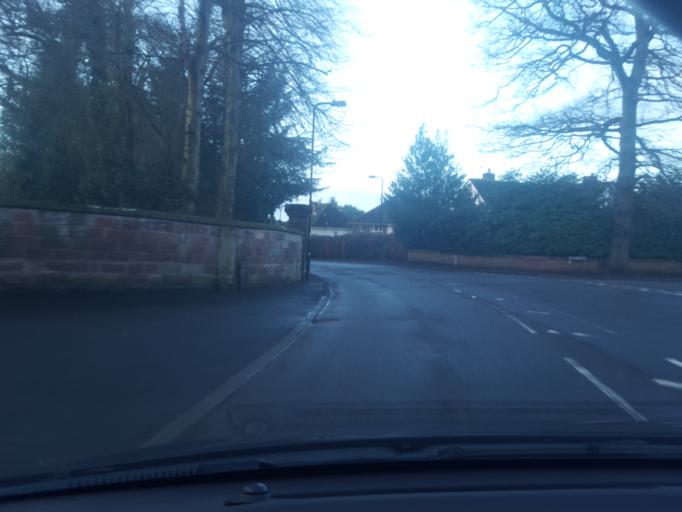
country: GB
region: England
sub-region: Shropshire
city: Albrighton
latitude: 52.6334
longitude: -2.2699
